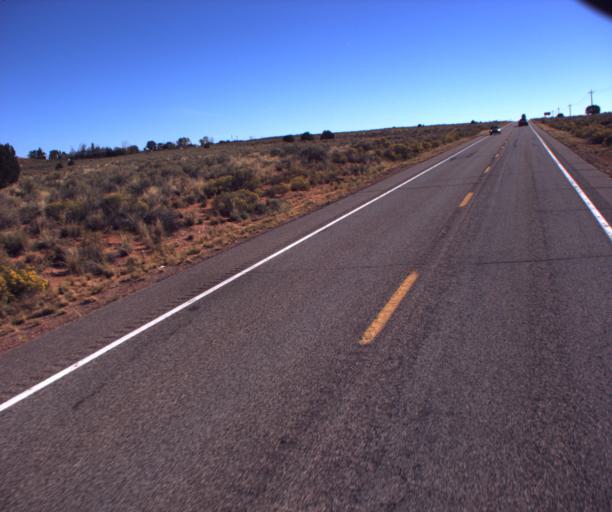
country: US
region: Arizona
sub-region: Coconino County
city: Fredonia
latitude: 36.8577
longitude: -112.7471
